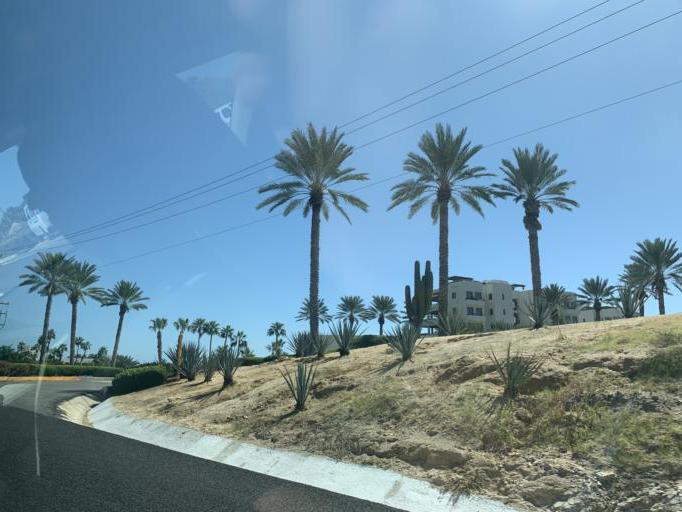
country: MX
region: Baja California Sur
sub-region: Los Cabos
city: San Jose del Cabo
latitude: 22.9797
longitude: -109.7710
